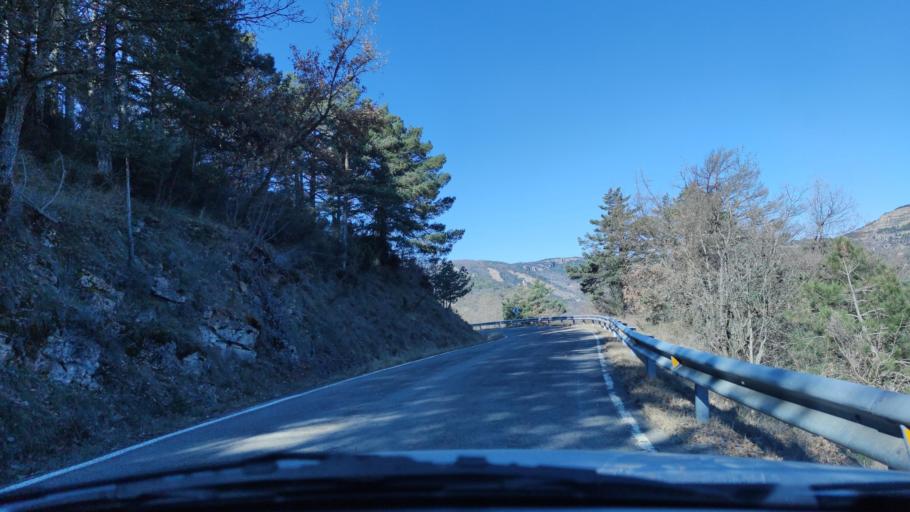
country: ES
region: Catalonia
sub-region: Provincia de Lleida
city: Llimiana
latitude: 42.0444
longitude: 1.0608
